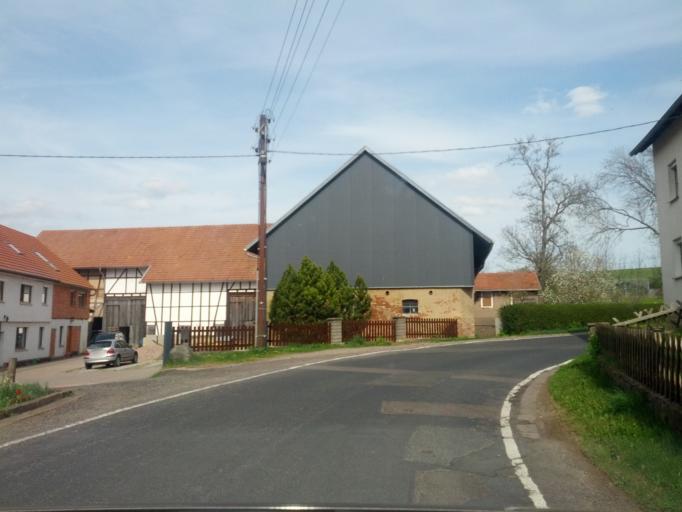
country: DE
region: Thuringia
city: Seebach
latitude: 50.9732
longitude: 10.4498
